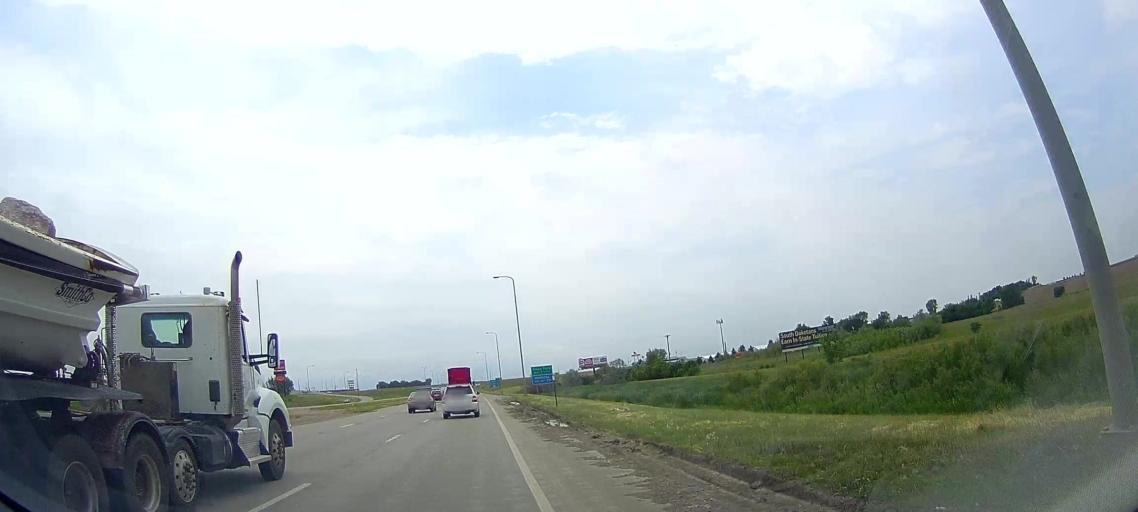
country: US
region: South Dakota
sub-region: Minnehaha County
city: Crooks
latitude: 43.6084
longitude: -96.7710
